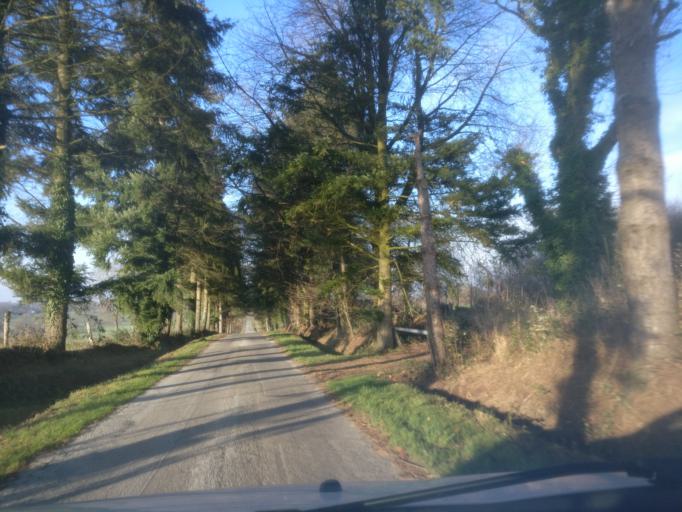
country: FR
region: Brittany
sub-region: Departement d'Ille-et-Vilaine
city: Livre-sur-Changeon
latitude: 48.1921
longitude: -1.3173
